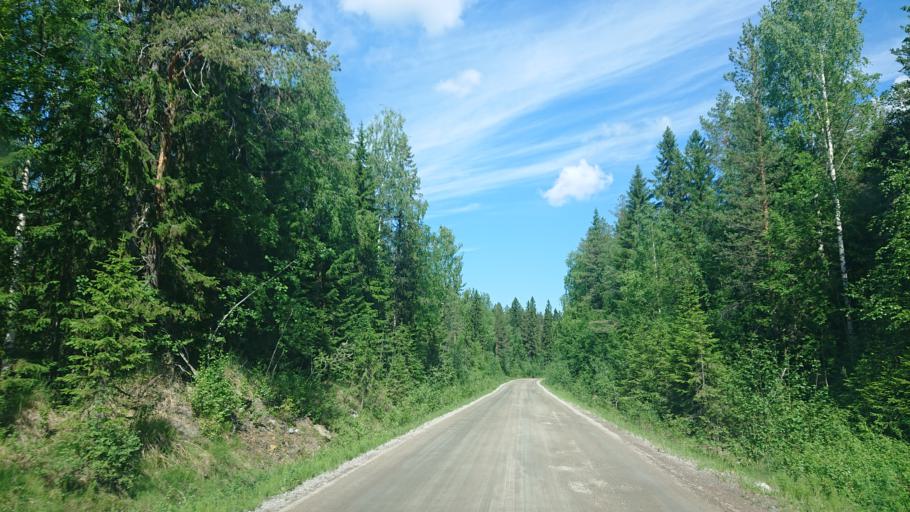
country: SE
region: Vaesternorrland
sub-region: Solleftea Kommun
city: Solleftea
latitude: 62.9578
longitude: 17.1462
